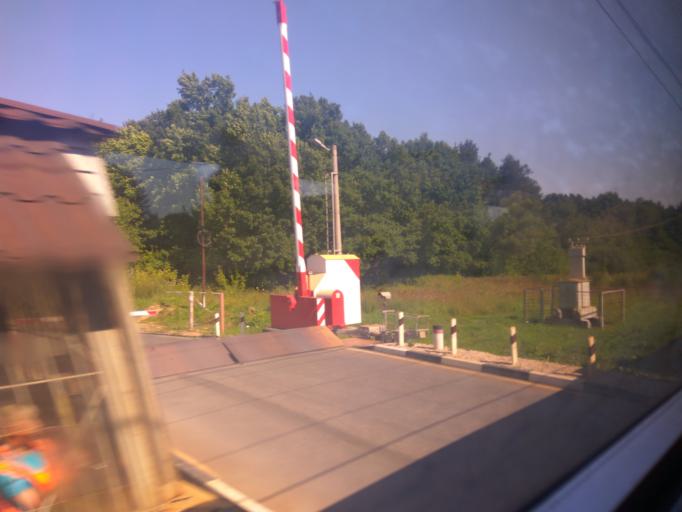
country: RU
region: Moskovskaya
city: Lesnoy Gorodok
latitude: 55.6661
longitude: 37.2188
